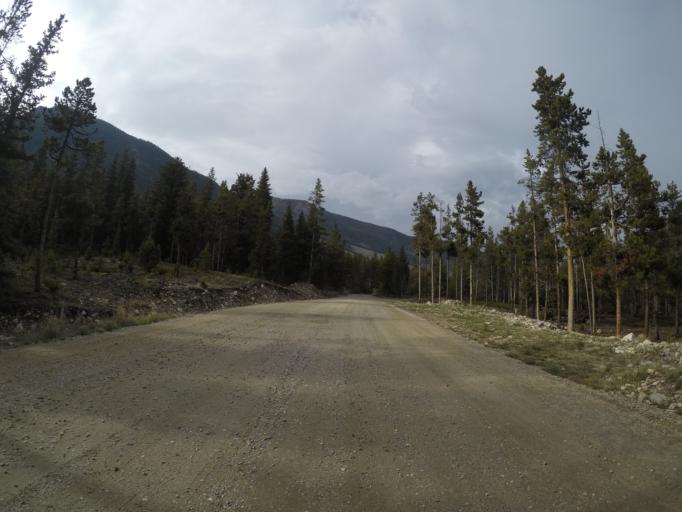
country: US
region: Montana
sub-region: Carbon County
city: Red Lodge
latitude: 45.0448
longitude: -109.4260
